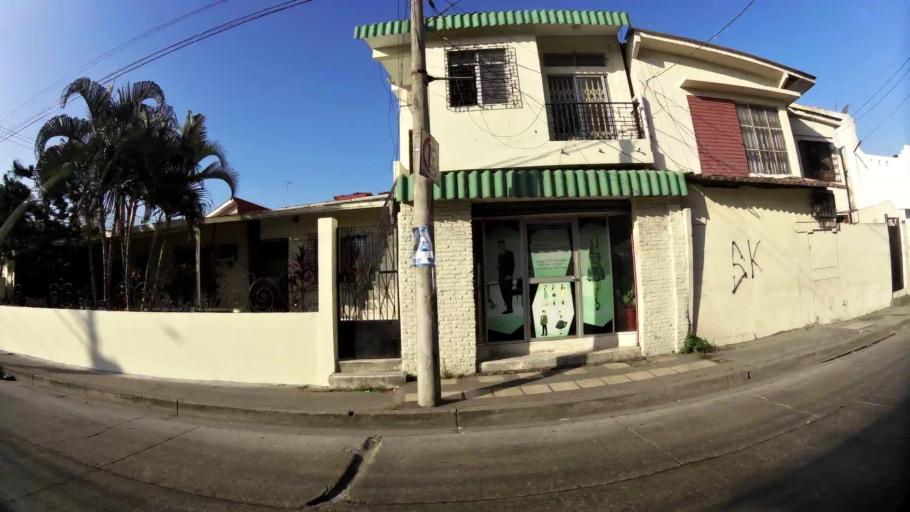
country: EC
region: Guayas
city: Guayaquil
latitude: -2.1612
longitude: -79.9181
